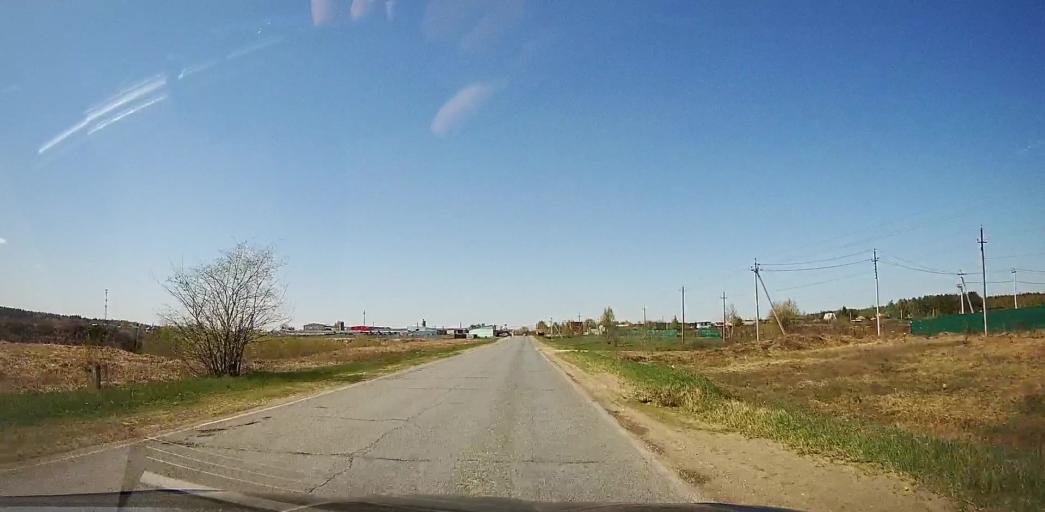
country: RU
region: Moskovskaya
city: Malyshevo
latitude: 55.4560
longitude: 38.3139
